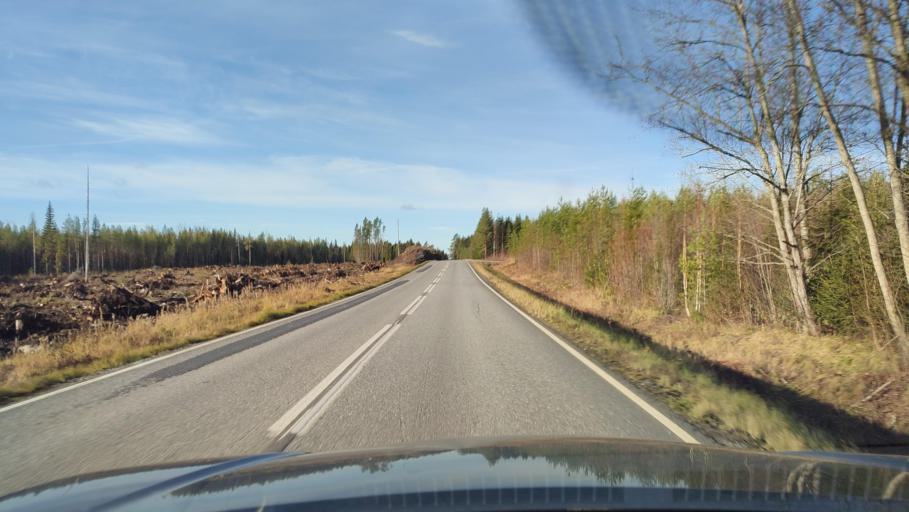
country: FI
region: Ostrobothnia
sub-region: Sydosterbotten
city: Naerpes
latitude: 62.4627
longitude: 21.5242
